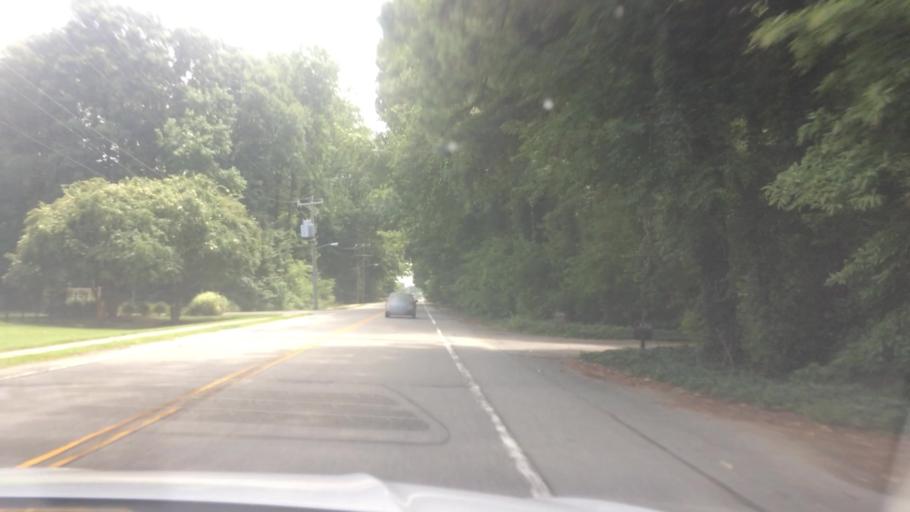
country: US
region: Virginia
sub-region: City of Williamsburg
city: Williamsburg
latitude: 37.2789
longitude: -76.6823
